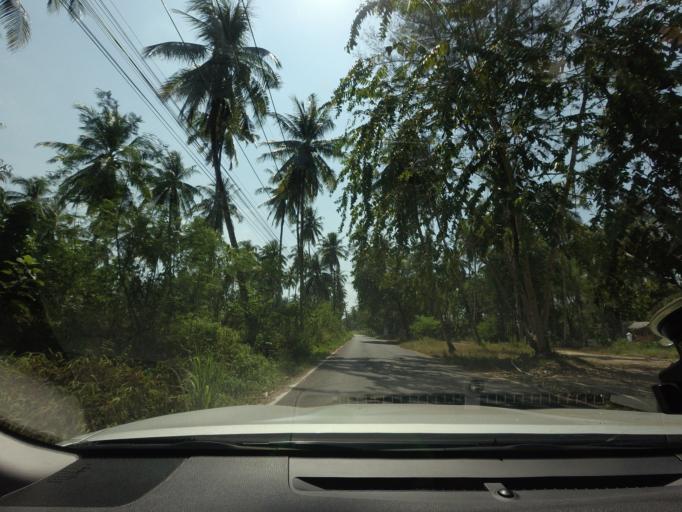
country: TH
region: Phangnga
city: Ban Khao Lak
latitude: 8.6951
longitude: 98.2444
